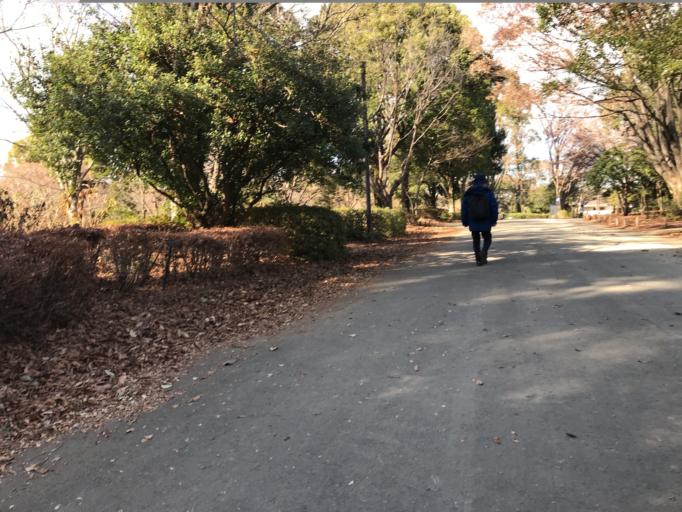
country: JP
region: Tokyo
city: Hino
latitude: 35.7063
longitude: 139.3970
